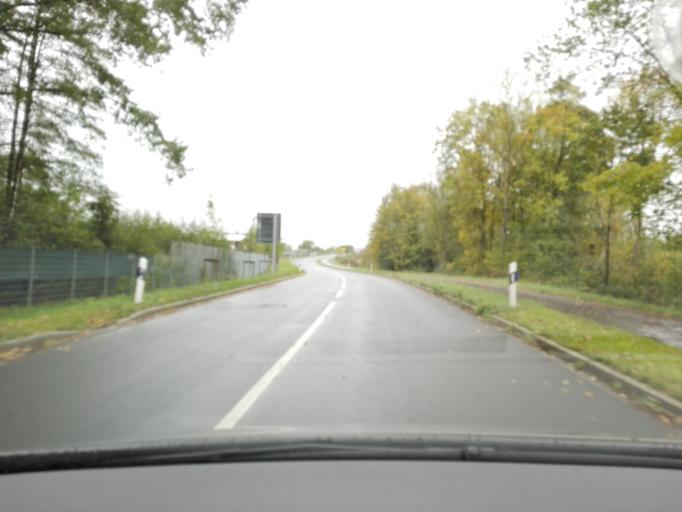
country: DE
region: North Rhine-Westphalia
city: Selm
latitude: 51.6909
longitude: 7.4870
